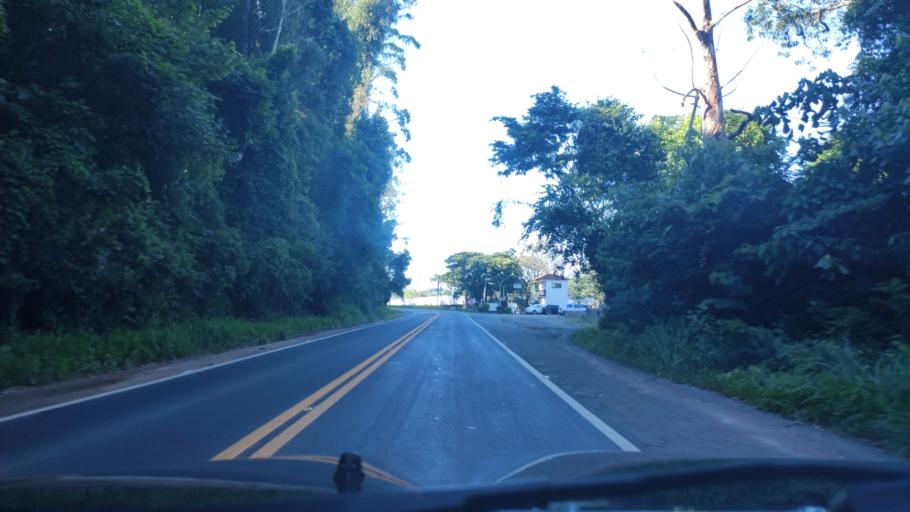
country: BR
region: Sao Paulo
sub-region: Socorro
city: Socorro
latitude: -22.6329
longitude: -46.5343
